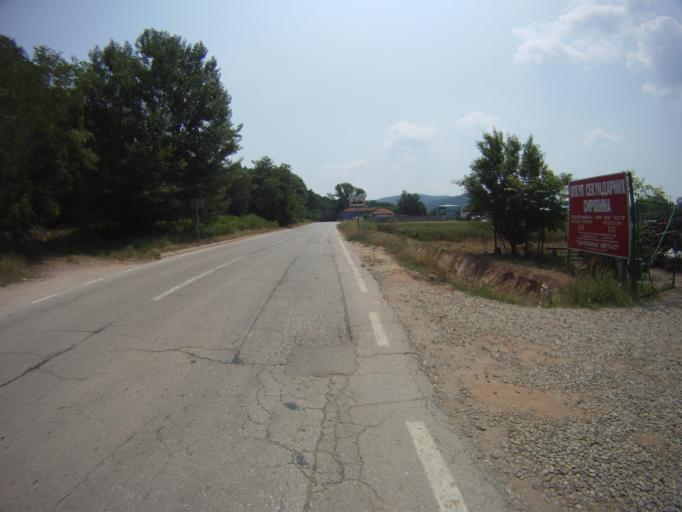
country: RS
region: Central Serbia
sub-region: Nisavski Okrug
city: Gadzin Han
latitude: 43.2311
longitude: 22.0306
